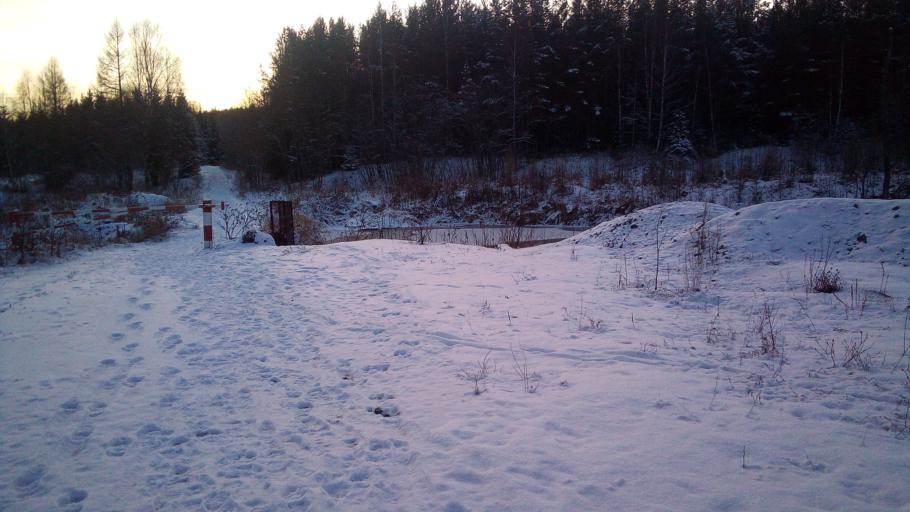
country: RU
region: Chelyabinsk
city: Bakal
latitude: 54.8147
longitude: 59.0007
